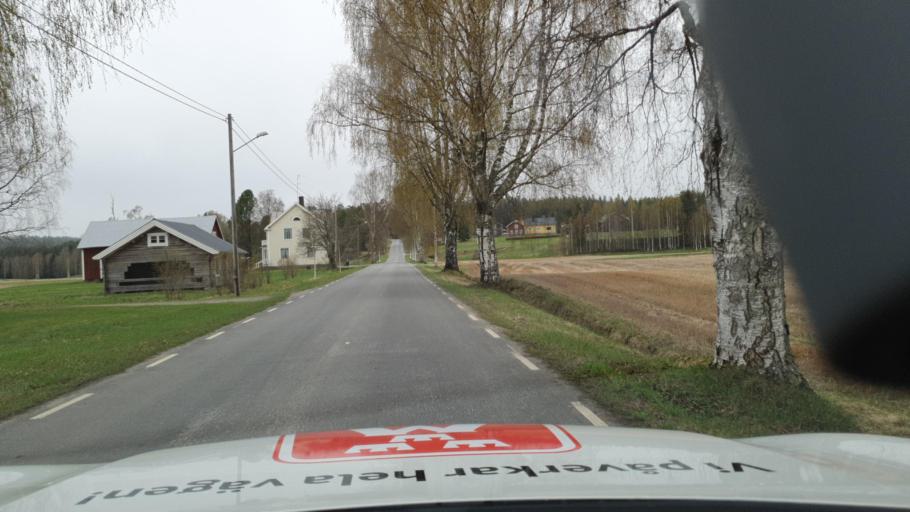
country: SE
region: Vaesterbotten
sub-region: Nordmalings Kommun
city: Nordmaling
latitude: 63.7261
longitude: 19.5121
